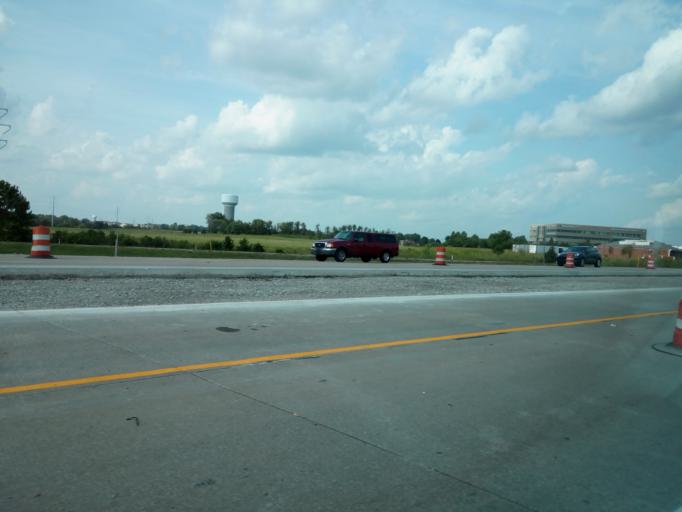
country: US
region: Kentucky
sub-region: Jefferson County
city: Anchorage
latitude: 38.2707
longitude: -85.4987
